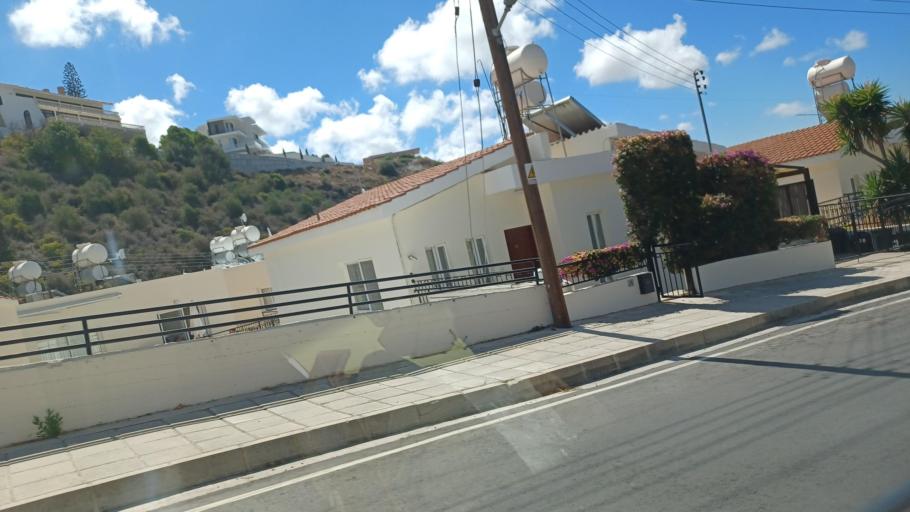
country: CY
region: Pafos
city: Tala
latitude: 34.8401
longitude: 32.4398
